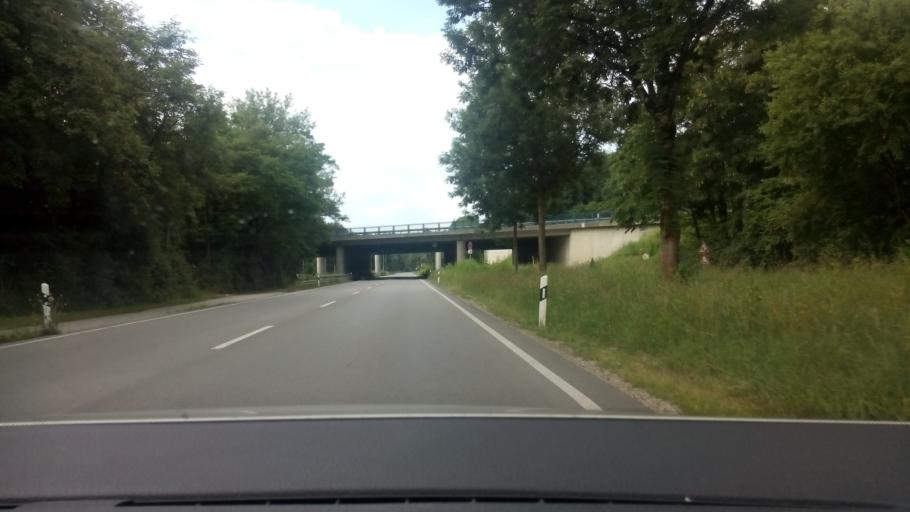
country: DE
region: Bavaria
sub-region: Upper Bavaria
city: Unterfoehring
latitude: 48.2186
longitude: 11.6370
